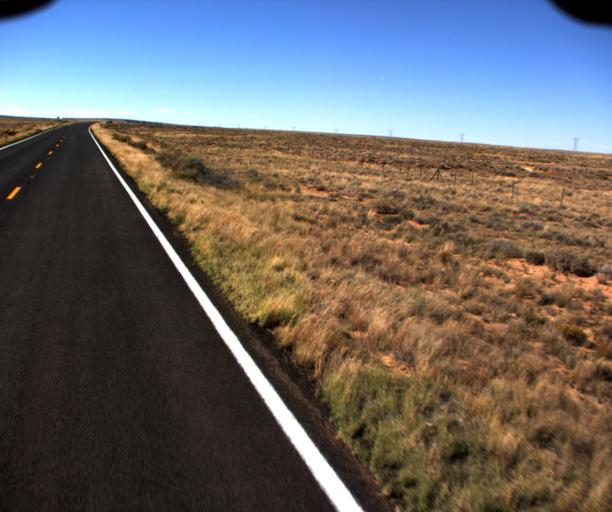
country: US
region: Arizona
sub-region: Navajo County
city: First Mesa
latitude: 35.9699
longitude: -110.7966
